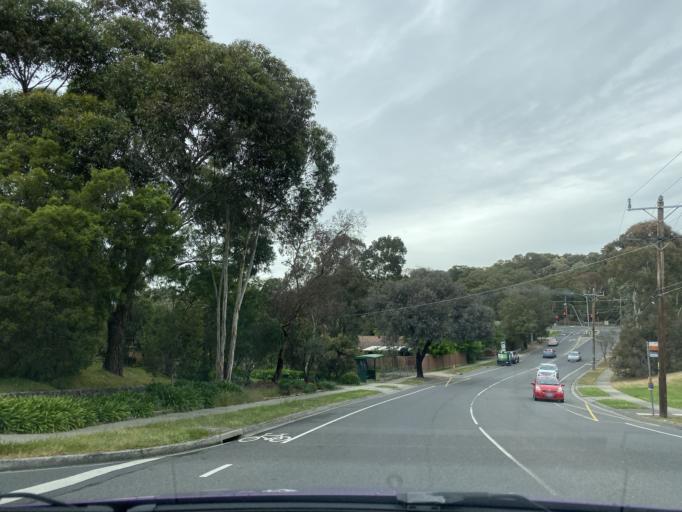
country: AU
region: Victoria
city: Saint Helena
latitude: -37.7032
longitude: 145.1283
